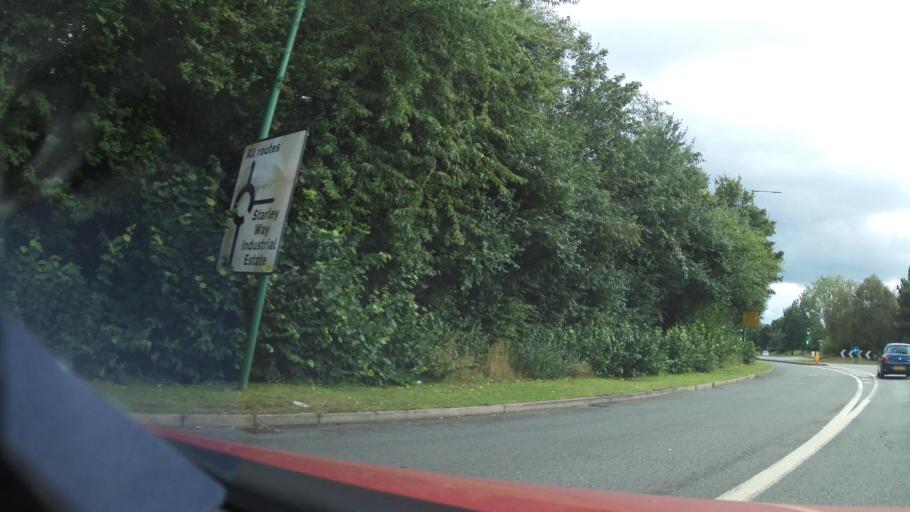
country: GB
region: England
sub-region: Solihull
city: Bickenhill
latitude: 52.4600
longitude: -1.7273
